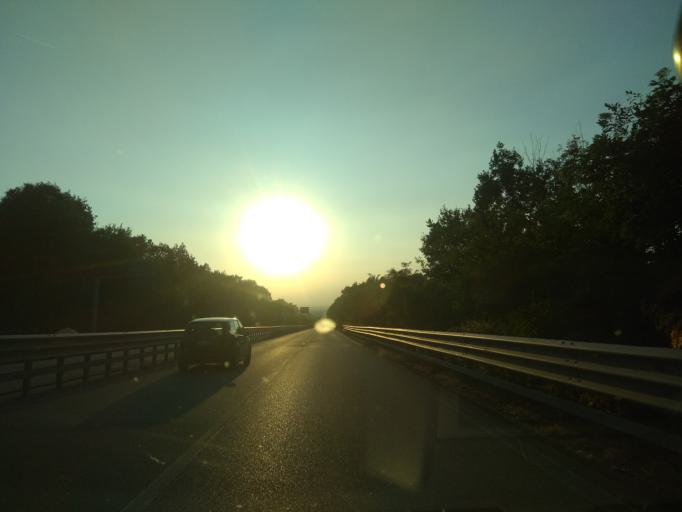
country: IT
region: Piedmont
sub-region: Provincia di Biella
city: Cossato
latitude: 45.5526
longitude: 8.2048
